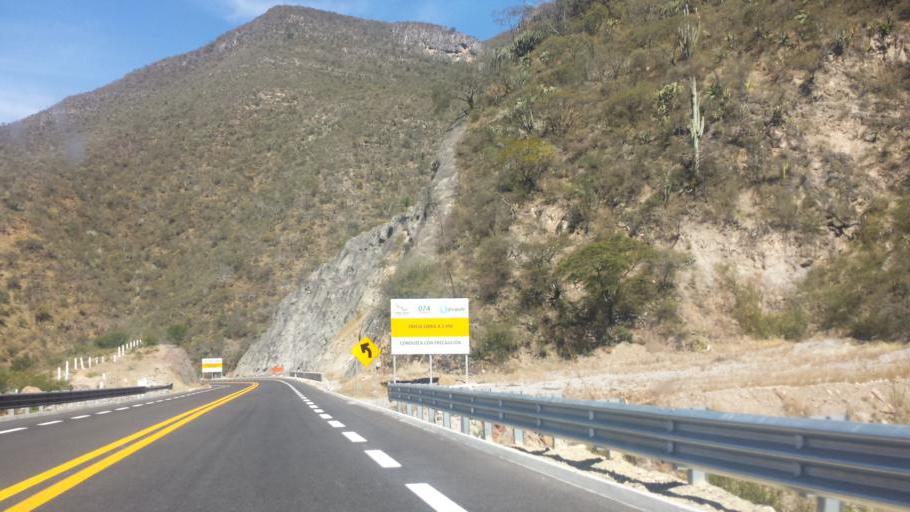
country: MX
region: Puebla
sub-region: San Jose Miahuatlan
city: San Pedro Tetitlan
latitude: 18.1020
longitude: -97.3360
